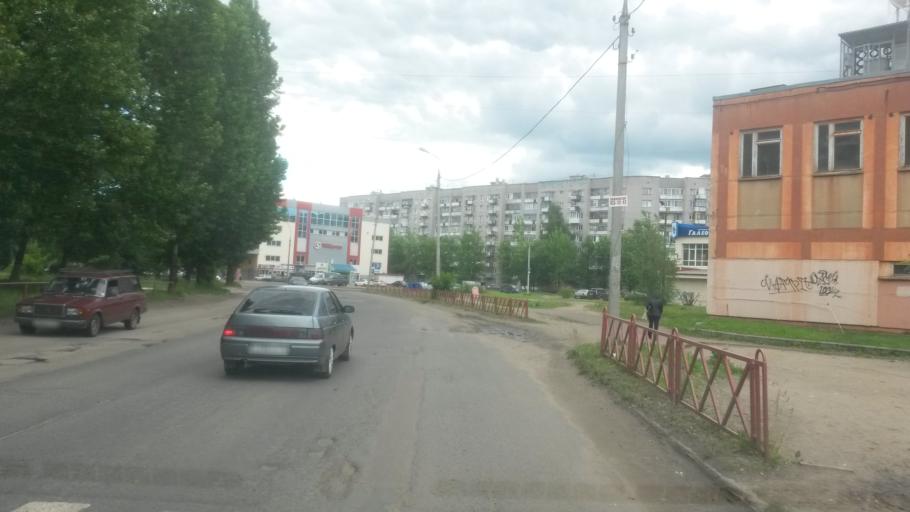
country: RU
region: Jaroslavl
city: Yaroslavl
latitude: 57.6784
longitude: 39.7861
